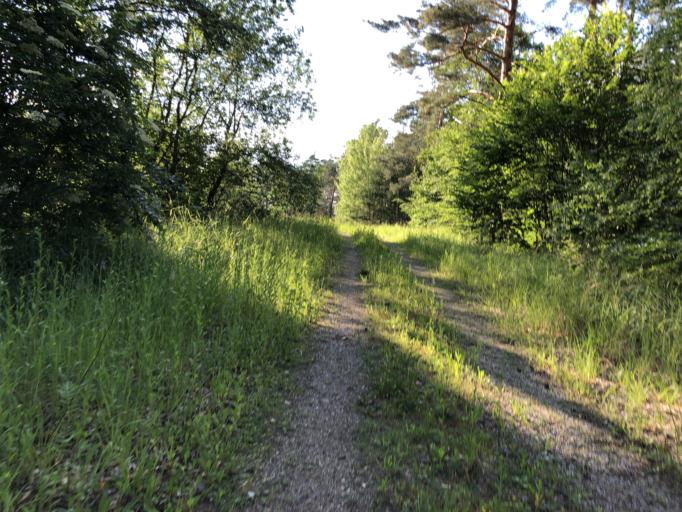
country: DE
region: Bavaria
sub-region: Upper Franconia
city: Memmelsdorf
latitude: 49.9142
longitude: 10.9528
